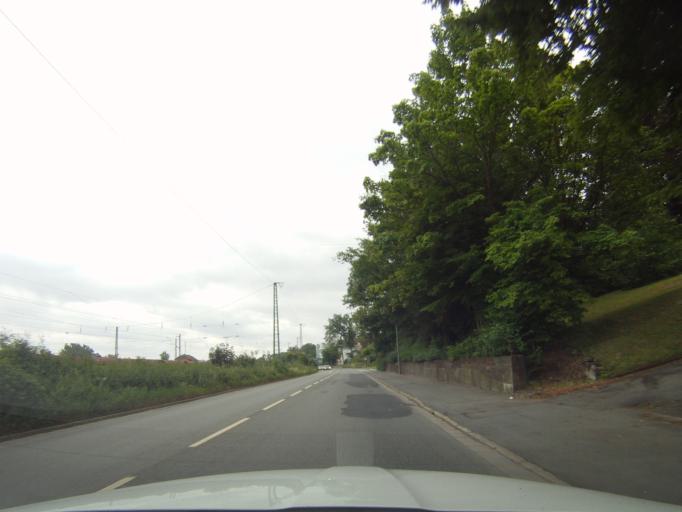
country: DE
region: Bavaria
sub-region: Upper Franconia
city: Coburg
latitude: 50.2490
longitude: 10.9593
